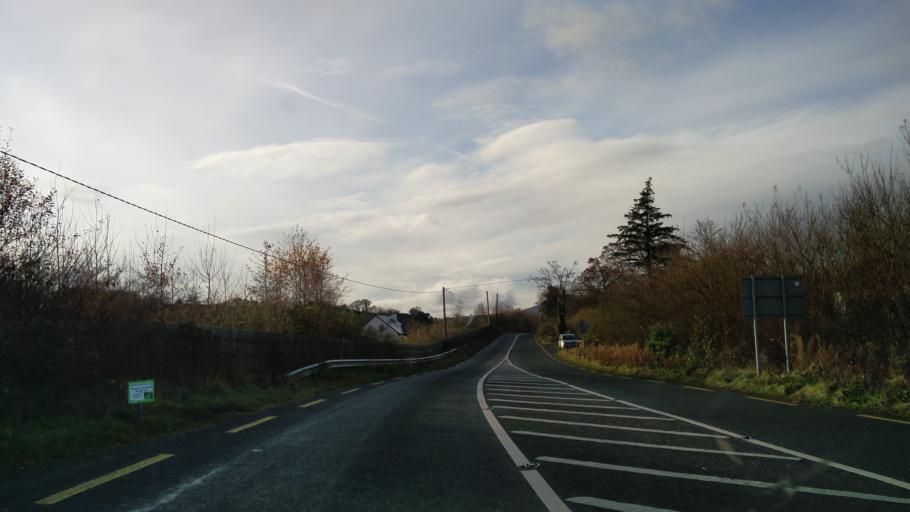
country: IE
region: Connaught
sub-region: Maigh Eo
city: Westport
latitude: 53.7840
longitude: -9.4730
